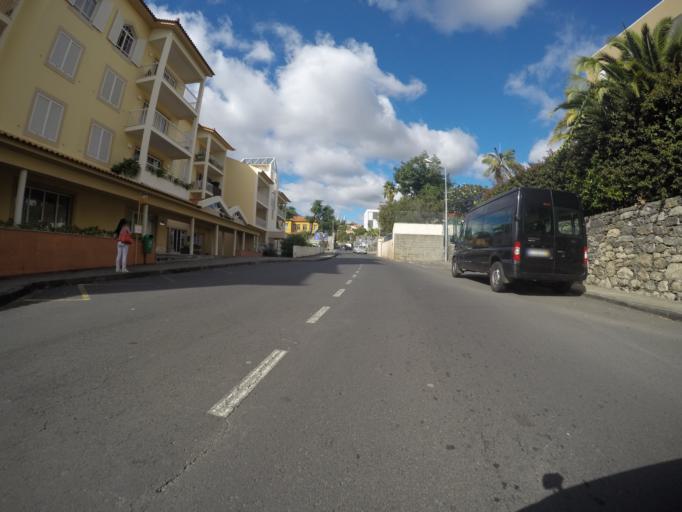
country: PT
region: Madeira
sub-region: Funchal
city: Nossa Senhora do Monte
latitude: 32.6608
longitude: -16.9321
